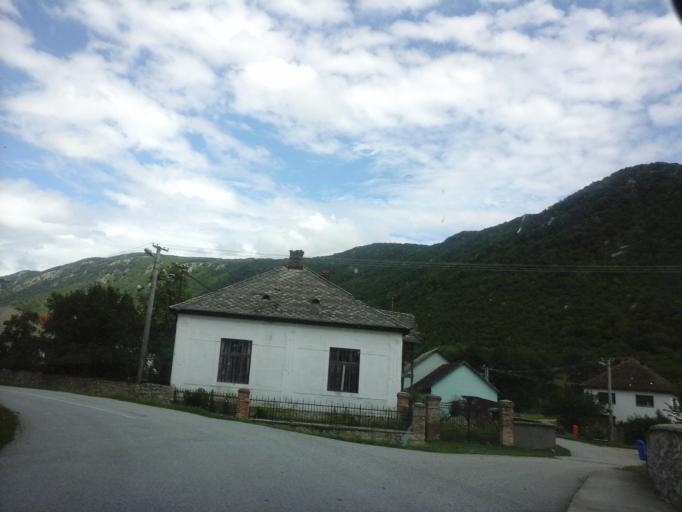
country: SK
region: Kosicky
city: Roznava
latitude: 48.5918
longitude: 20.3843
